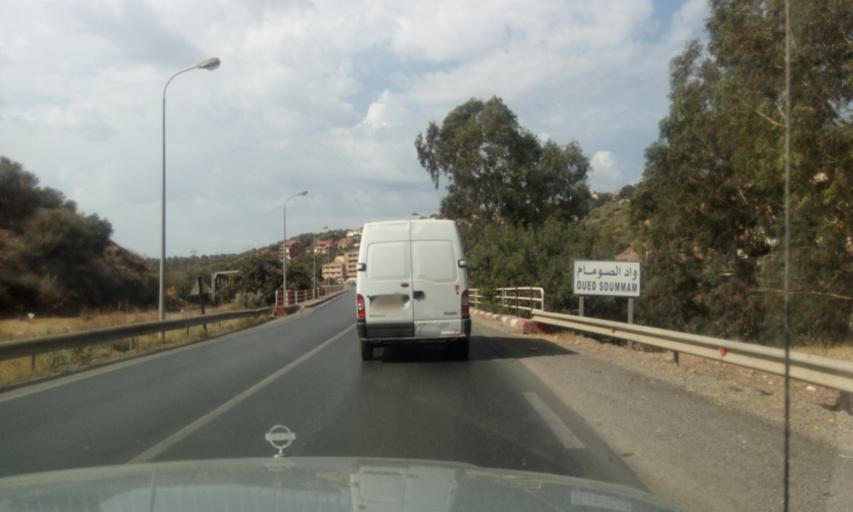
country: DZ
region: Bejaia
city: Seddouk
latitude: 36.6103
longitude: 4.6852
